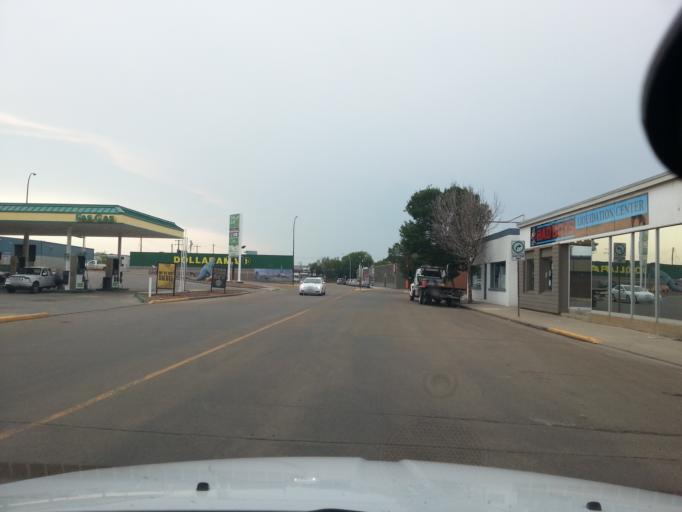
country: CA
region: Alberta
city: Three Hills
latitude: 51.4627
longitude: -112.7094
